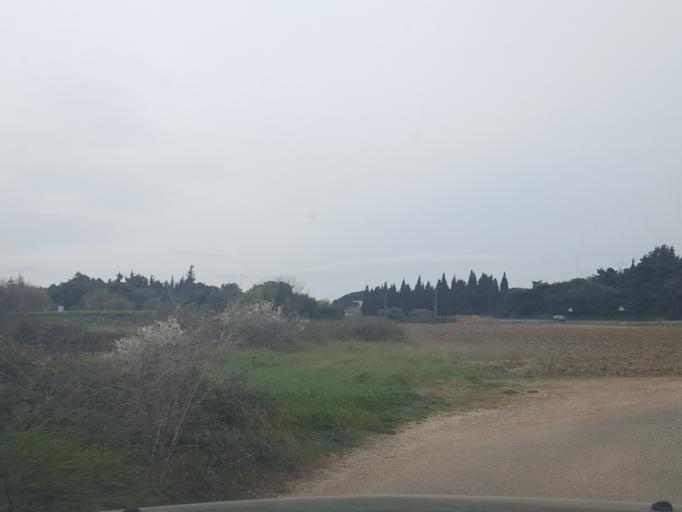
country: FR
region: Provence-Alpes-Cote d'Azur
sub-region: Departement du Vaucluse
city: Saint-Saturnin-les-Avignon
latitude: 43.9514
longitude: 4.9143
